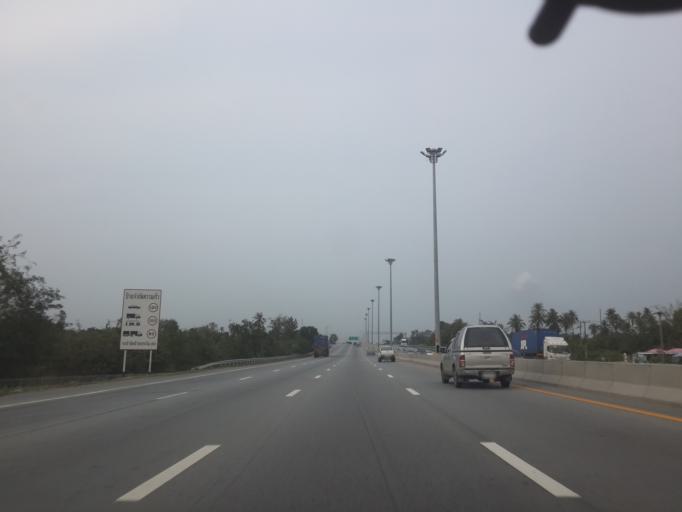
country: TH
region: Chon Buri
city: Chon Buri
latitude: 13.3141
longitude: 101.0069
